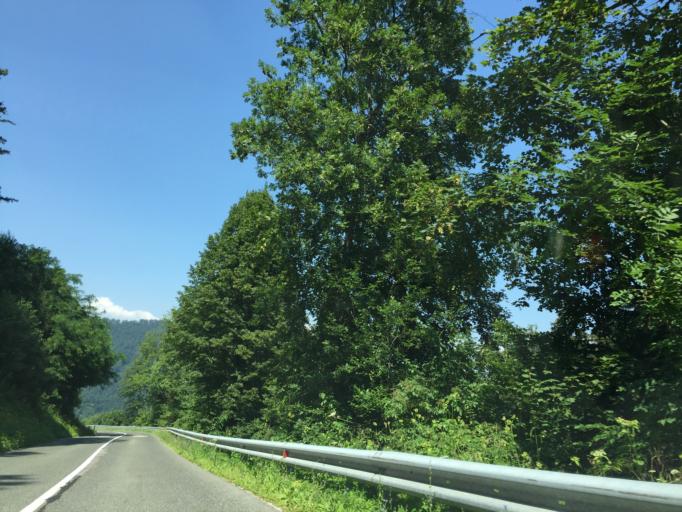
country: SI
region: Trbovlje
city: Trbovlje
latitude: 46.1881
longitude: 15.0627
